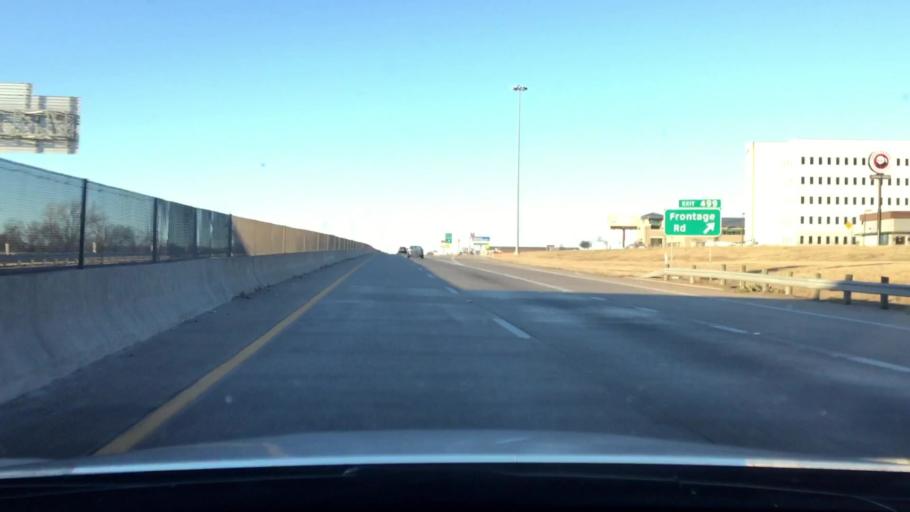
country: US
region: Texas
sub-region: Cooke County
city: Gainesville
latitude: 33.6409
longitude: -97.1557
